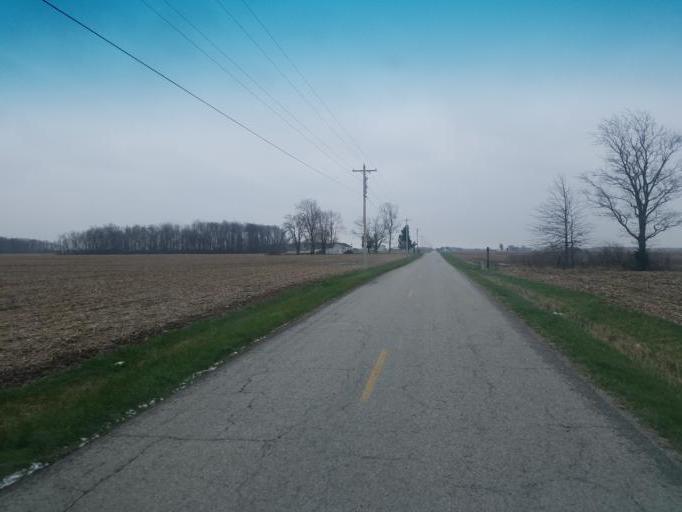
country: US
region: Ohio
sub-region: Marion County
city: Prospect
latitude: 40.4004
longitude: -83.1171
